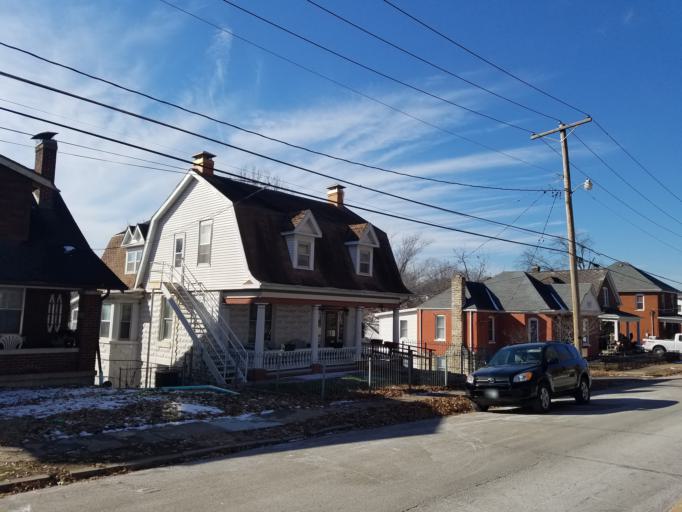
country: US
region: Missouri
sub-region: Cole County
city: Jefferson City
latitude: 38.5875
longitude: -92.1866
